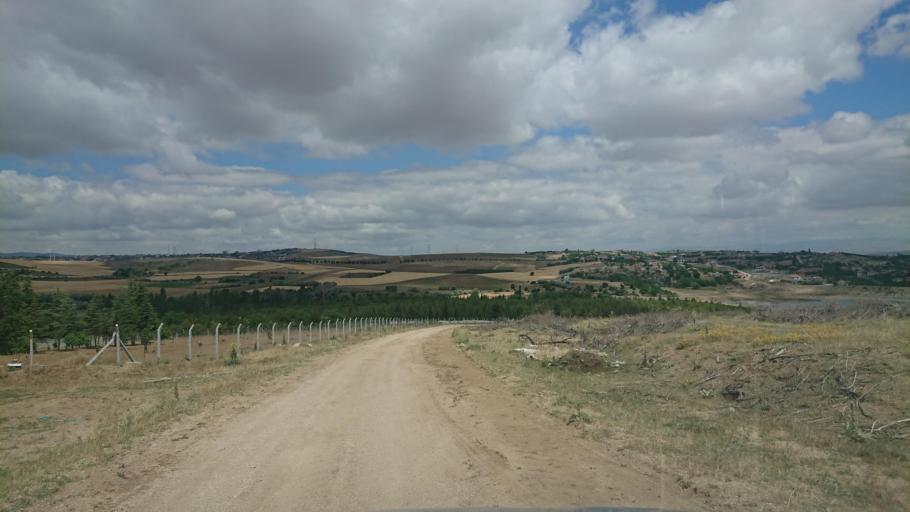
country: TR
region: Aksaray
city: Agacoren
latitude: 38.8579
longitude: 33.9487
